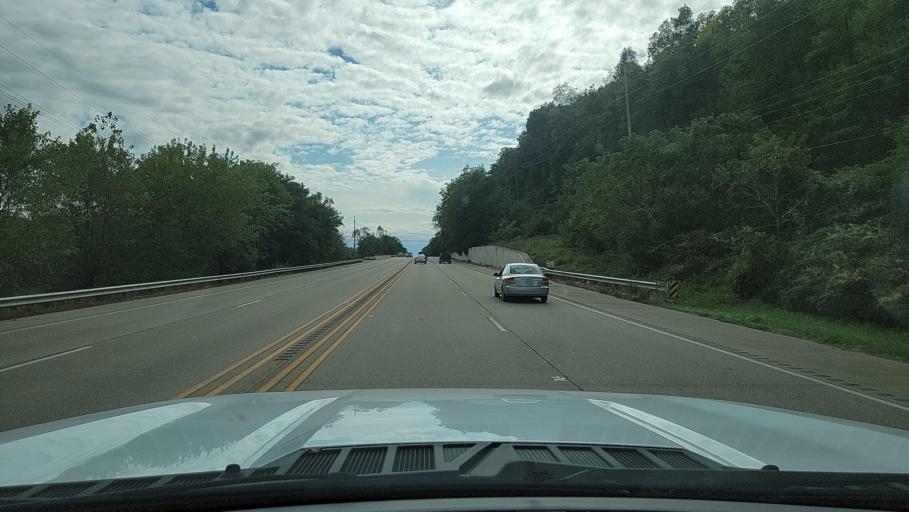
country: US
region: Illinois
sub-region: Peoria County
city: Bartonville
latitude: 40.6249
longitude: -89.6544
